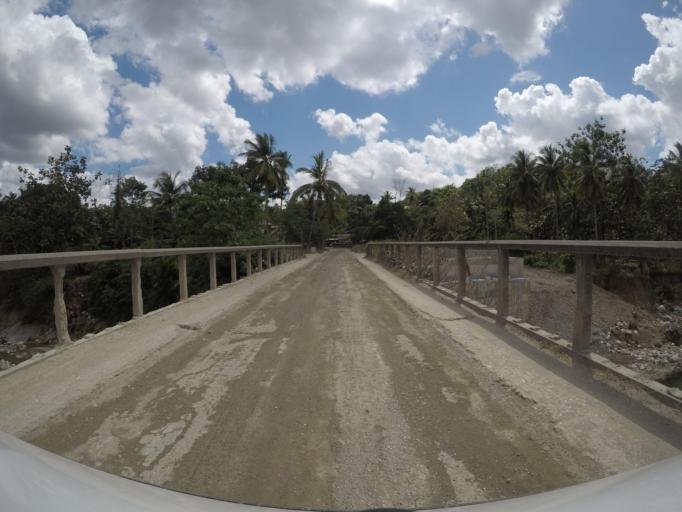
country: TL
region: Viqueque
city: Viqueque
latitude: -8.8343
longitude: 126.3729
